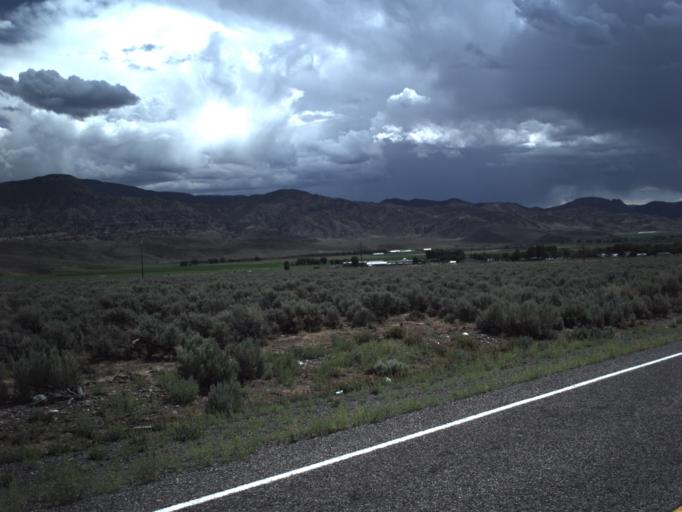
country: US
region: Utah
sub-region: Piute County
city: Junction
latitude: 38.2496
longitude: -112.2382
